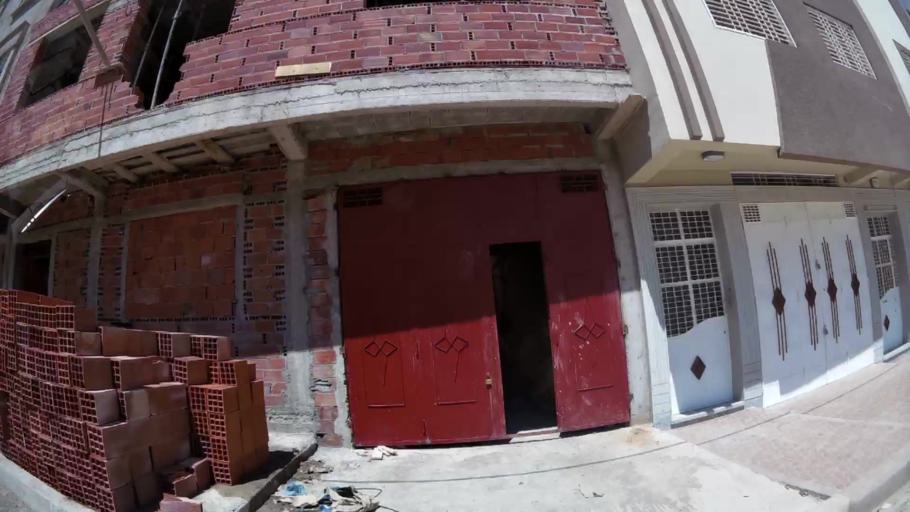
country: MA
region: Oriental
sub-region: Oujda-Angad
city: Oujda
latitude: 34.6813
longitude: -1.9479
